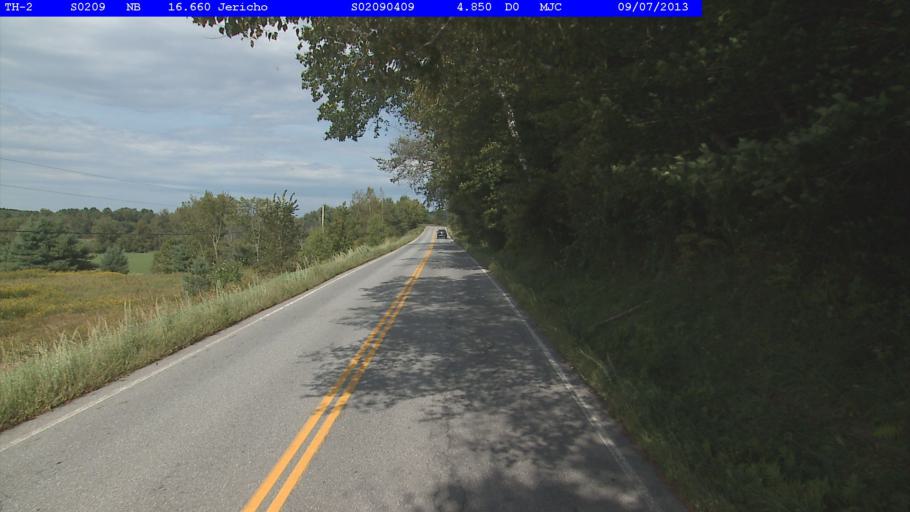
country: US
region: Vermont
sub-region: Chittenden County
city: Jericho
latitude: 44.4919
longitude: -72.9838
